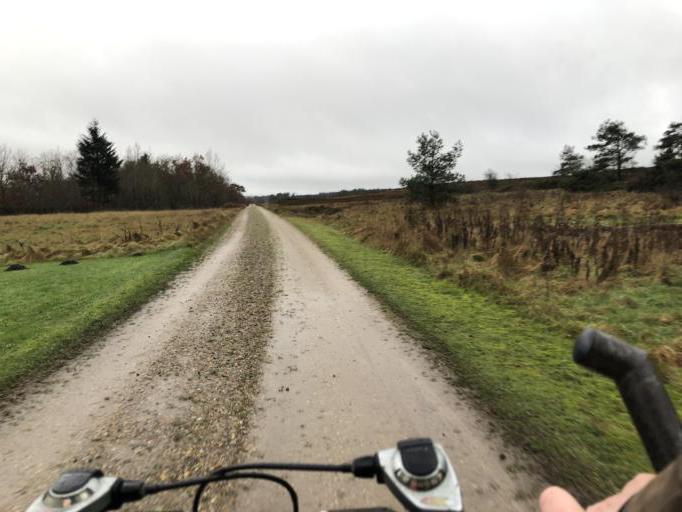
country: DK
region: Central Jutland
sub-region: Holstebro Kommune
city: Ulfborg
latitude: 56.2871
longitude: 8.4599
